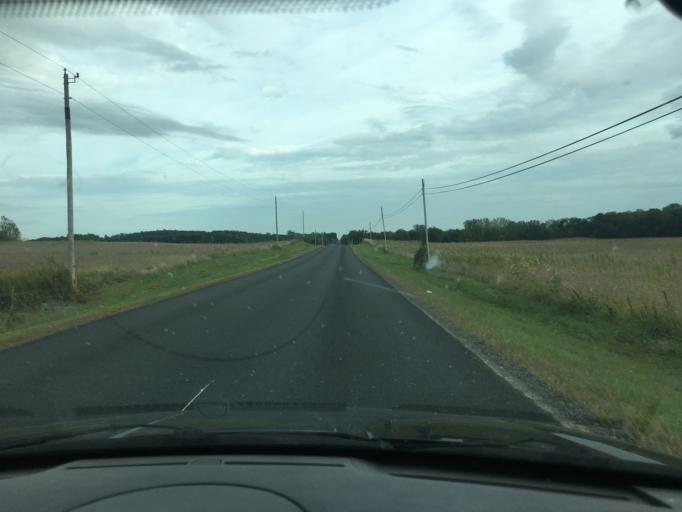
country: US
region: Ohio
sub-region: Logan County
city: Bellefontaine
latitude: 40.3259
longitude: -83.7357
